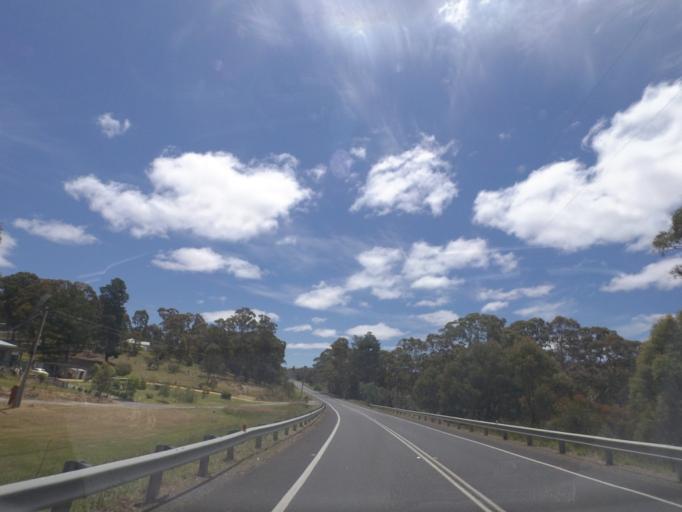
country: AU
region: Victoria
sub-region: Mount Alexander
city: Castlemaine
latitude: -37.2893
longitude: 144.1631
